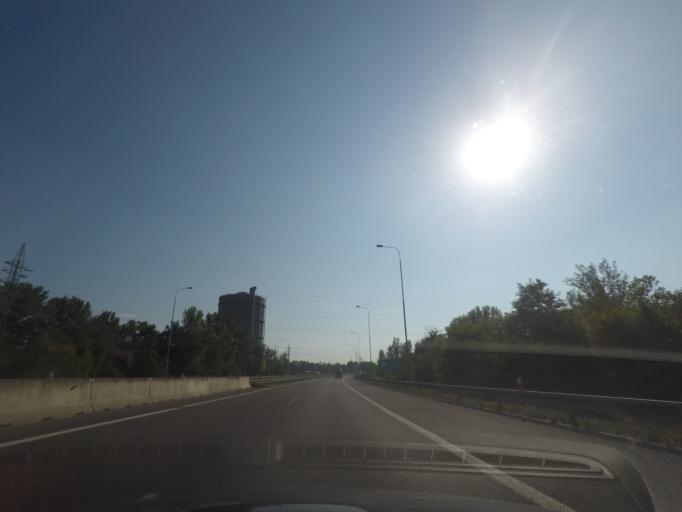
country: CZ
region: Moravskoslezsky
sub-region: Okres Ostrava-Mesto
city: Ostrava
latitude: 49.8657
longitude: 18.2751
